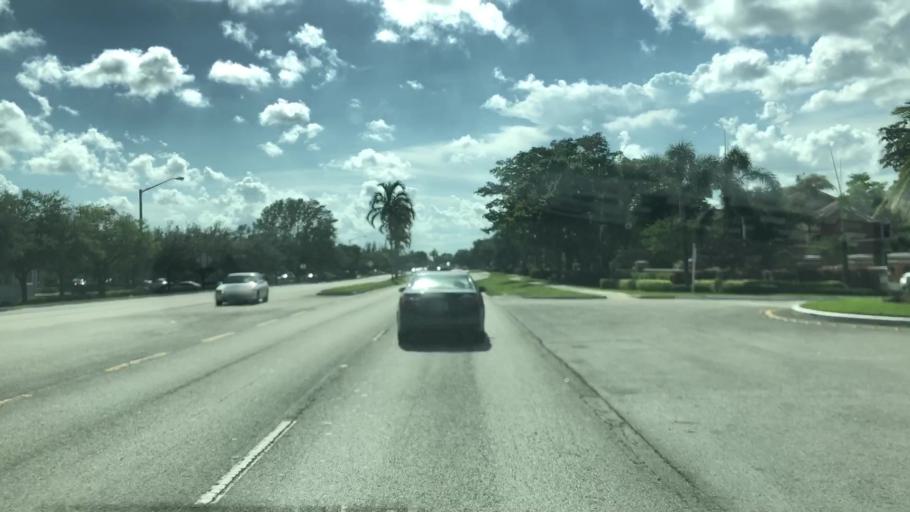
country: US
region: Florida
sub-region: Broward County
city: Parkland
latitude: 26.2870
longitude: -80.2458
